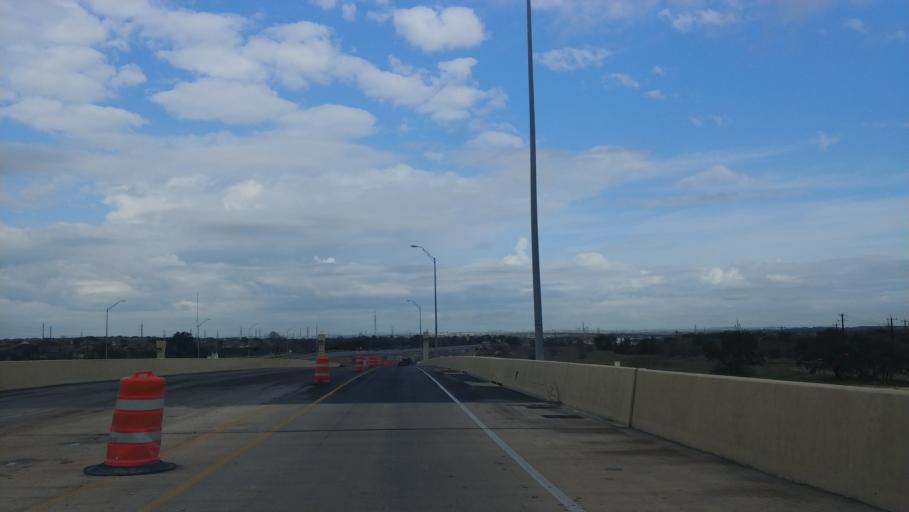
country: US
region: Texas
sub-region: Bexar County
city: Lackland Air Force Base
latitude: 29.4037
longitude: -98.7067
